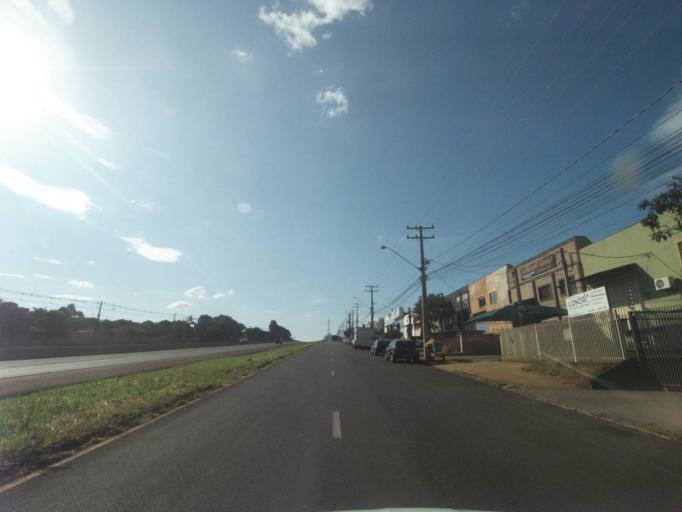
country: BR
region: Parana
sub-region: Londrina
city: Londrina
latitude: -23.3529
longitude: -51.1622
